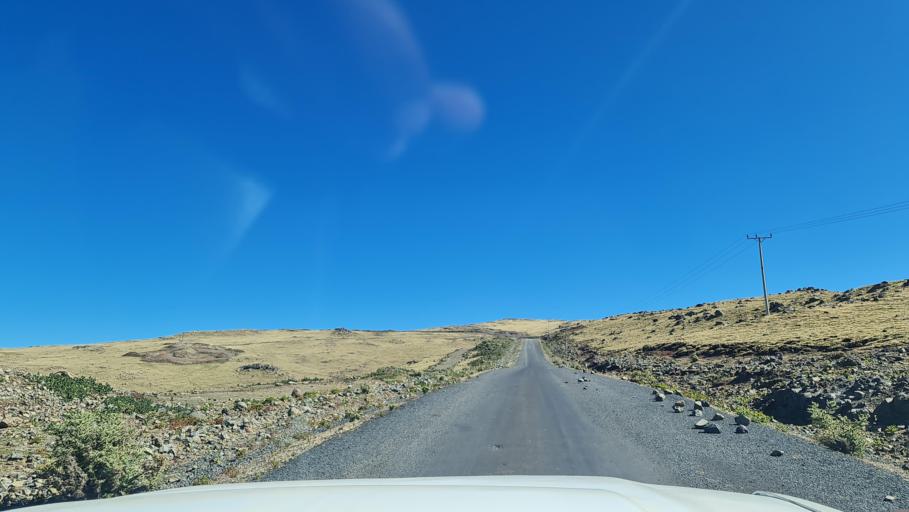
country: ET
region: Amhara
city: Debark'
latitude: 13.1421
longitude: 38.1784
